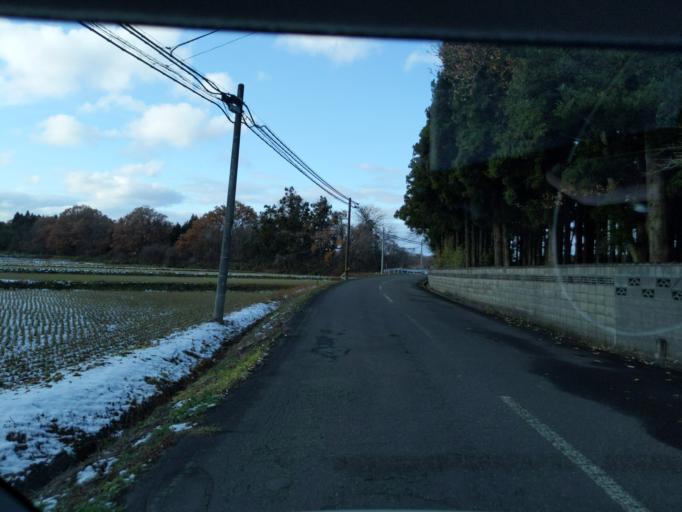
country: JP
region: Iwate
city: Kitakami
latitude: 39.2217
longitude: 141.0444
